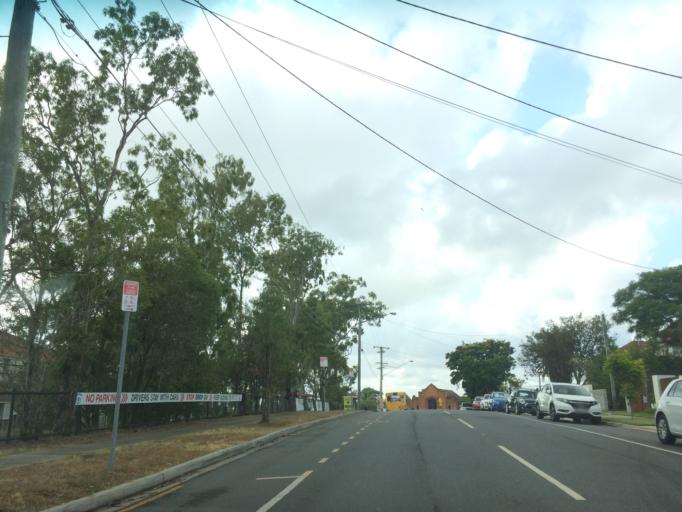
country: AU
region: Queensland
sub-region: Brisbane
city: Toowong
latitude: -27.4997
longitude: 152.9952
